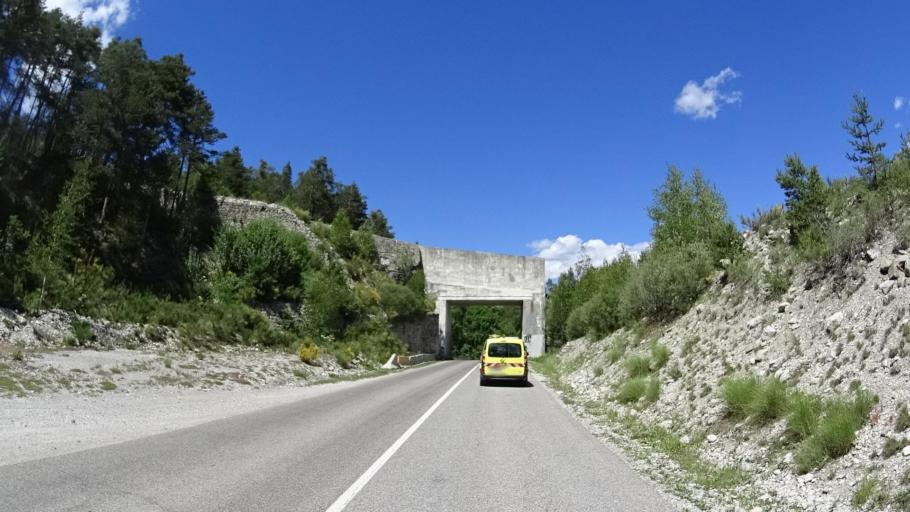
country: FR
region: Provence-Alpes-Cote d'Azur
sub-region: Departement des Alpes-de-Haute-Provence
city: Annot
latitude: 44.1295
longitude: 6.5807
